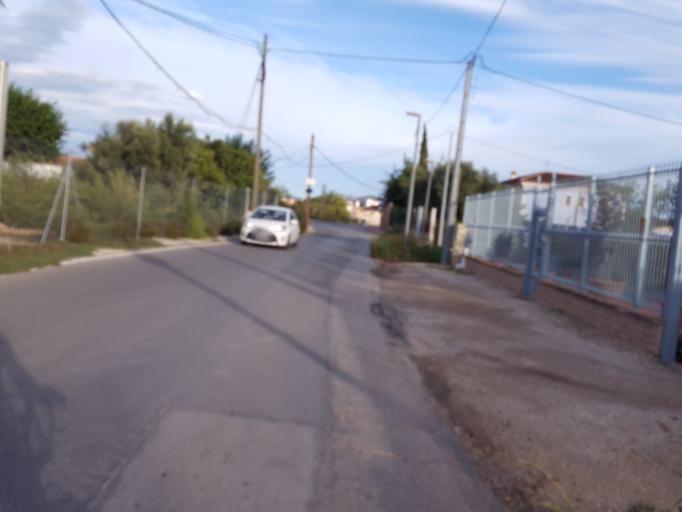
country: ES
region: Murcia
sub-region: Murcia
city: Murcia
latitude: 37.9892
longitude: -1.1652
